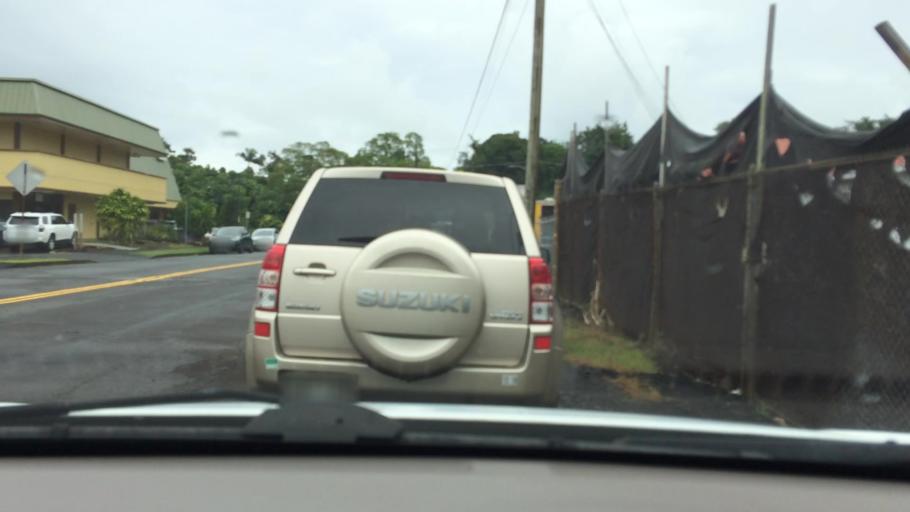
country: US
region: Hawaii
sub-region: Hawaii County
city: Hilo
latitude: 19.7212
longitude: -155.0653
